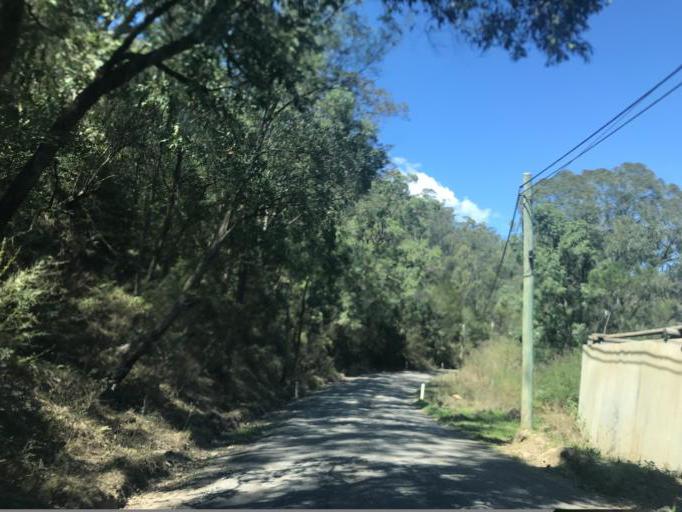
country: AU
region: New South Wales
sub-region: Hornsby Shire
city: Glenorie
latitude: -33.2845
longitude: 150.9694
